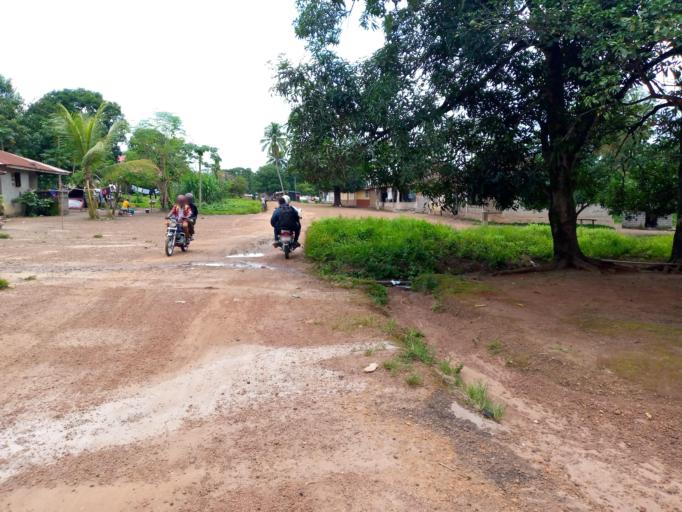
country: SL
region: Northern Province
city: Magburaka
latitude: 8.7102
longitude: -11.9314
